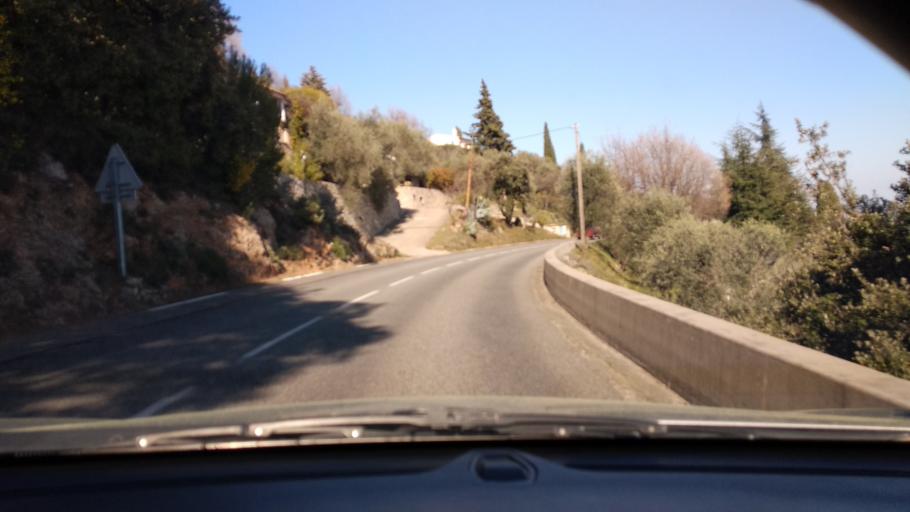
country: FR
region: Provence-Alpes-Cote d'Azur
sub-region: Departement des Alpes-Maritimes
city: Le Tignet
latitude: 43.6373
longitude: 6.8370
